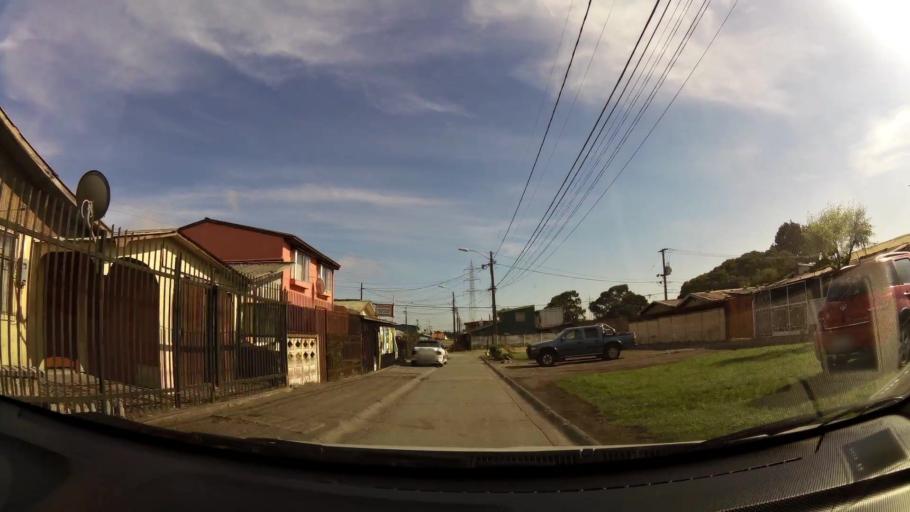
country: CL
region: Biobio
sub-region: Provincia de Concepcion
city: Talcahuano
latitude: -36.7779
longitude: -73.1148
